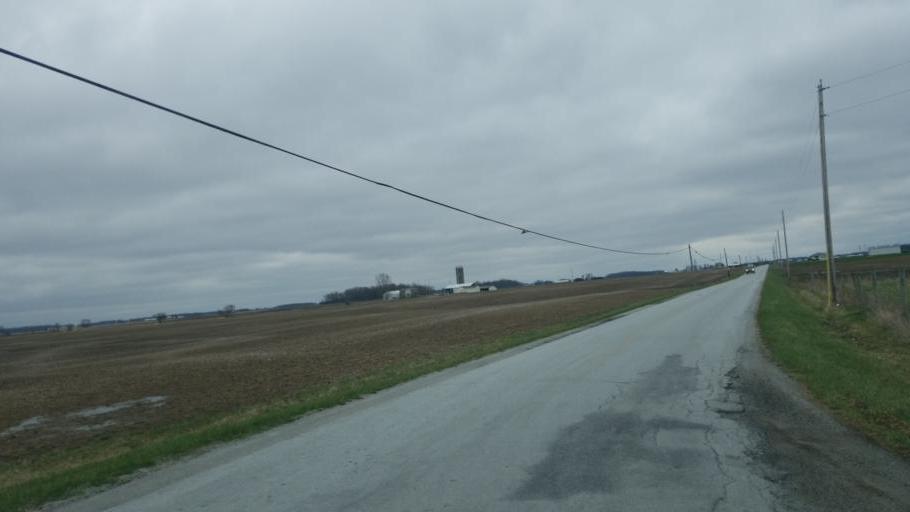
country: US
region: Ohio
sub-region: Hardin County
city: Kenton
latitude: 40.6585
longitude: -83.5379
